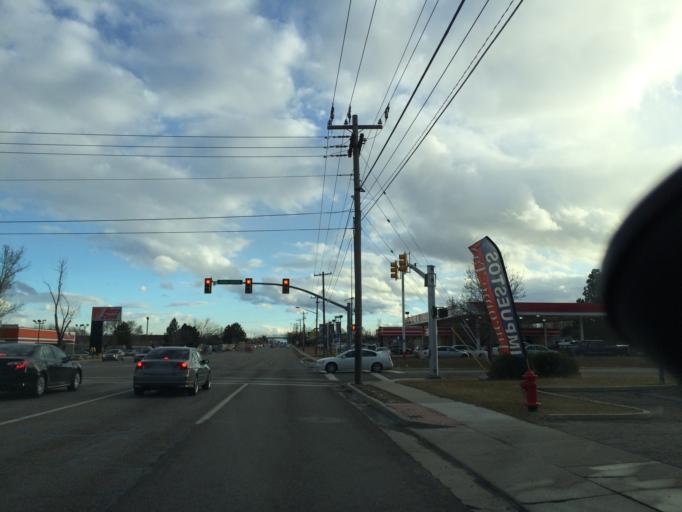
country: US
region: Utah
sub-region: Salt Lake County
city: Taylorsville
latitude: 40.6800
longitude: -111.9390
